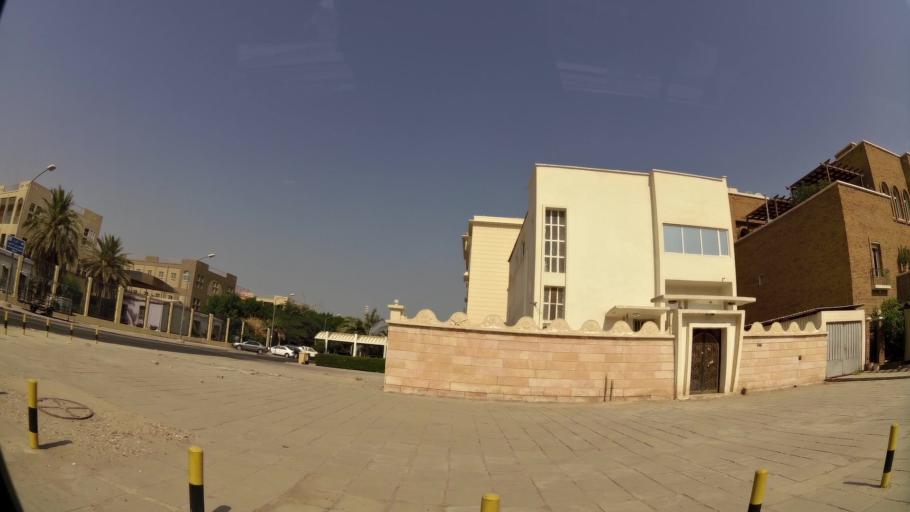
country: KW
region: Muhafazat Hawalli
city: Hawalli
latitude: 29.3503
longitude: 48.0182
